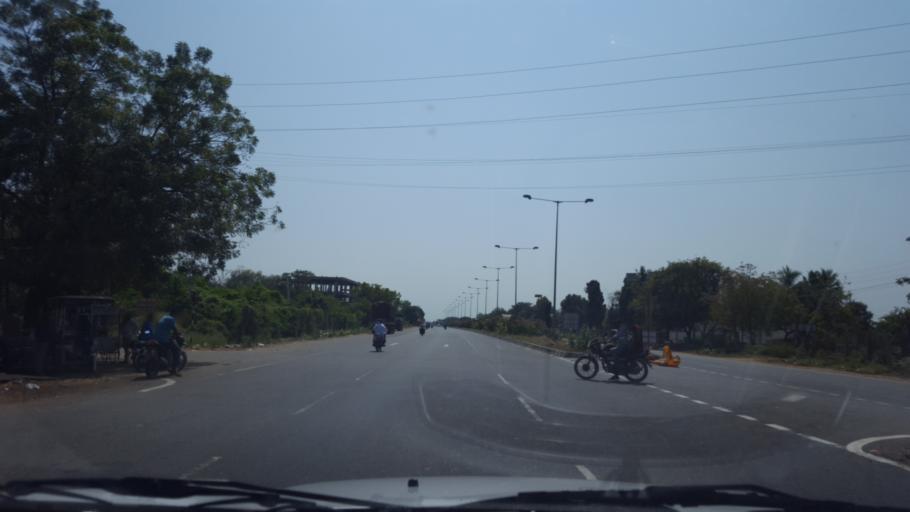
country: IN
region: Andhra Pradesh
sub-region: Prakasam
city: Ongole
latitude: 15.6031
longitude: 80.0294
